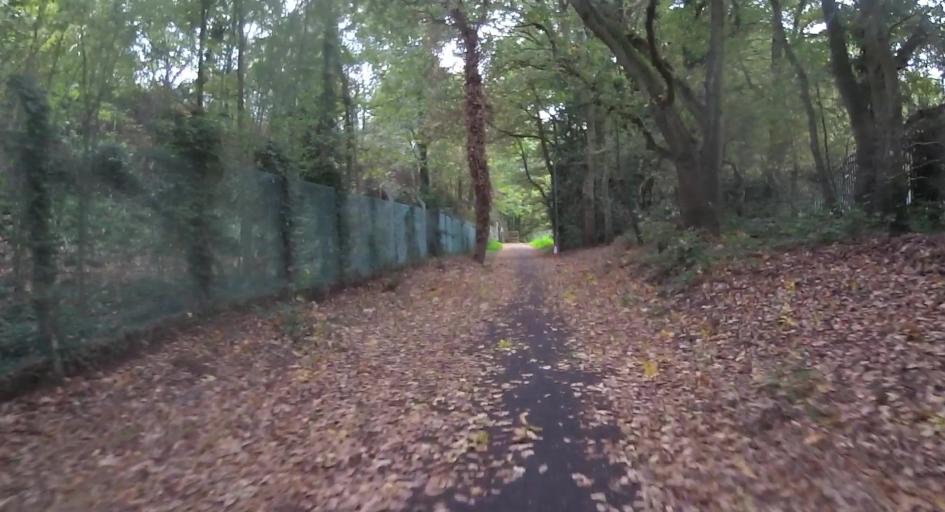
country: GB
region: England
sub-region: Surrey
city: Byfleet
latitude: 51.3575
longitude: -0.4663
